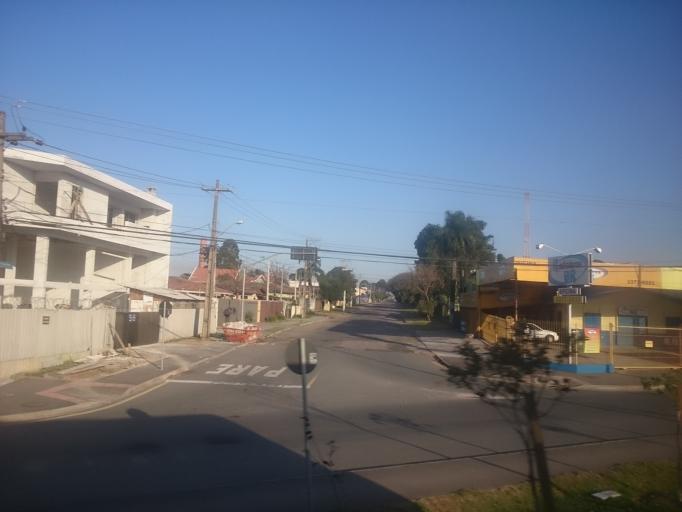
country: BR
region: Parana
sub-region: Curitiba
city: Curitiba
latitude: -25.4787
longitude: -49.2613
